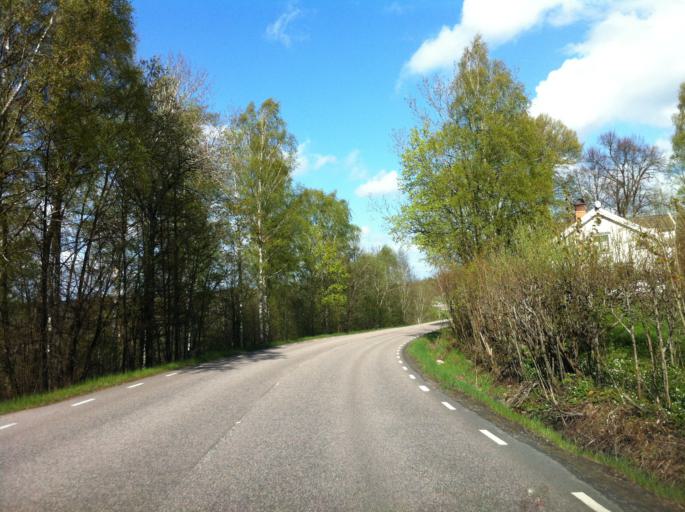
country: SE
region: Vaestra Goetaland
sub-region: Alingsas Kommun
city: Alingsas
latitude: 57.8597
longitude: 12.5602
